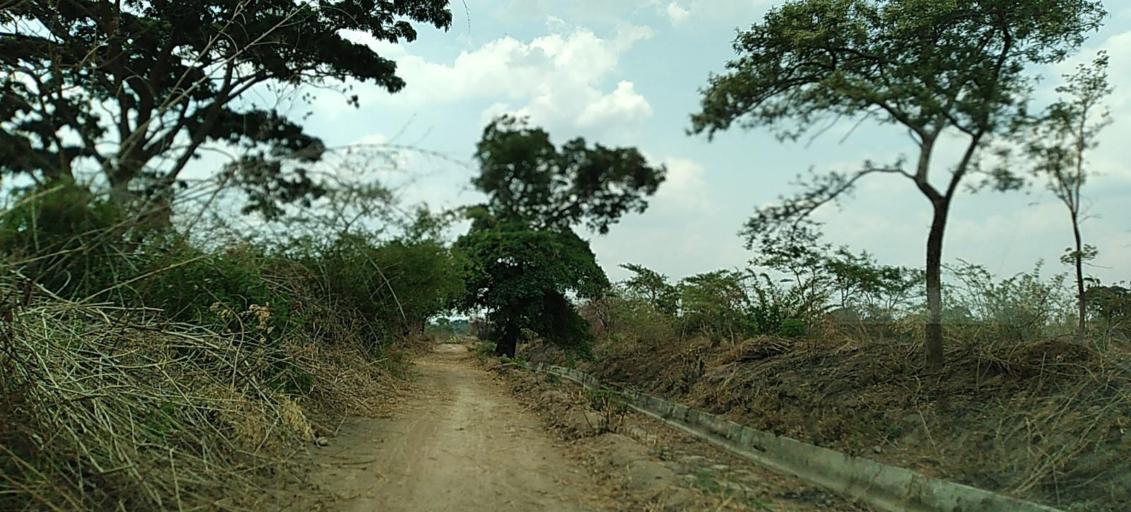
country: ZM
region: Copperbelt
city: Chililabombwe
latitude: -12.3561
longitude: 27.8041
